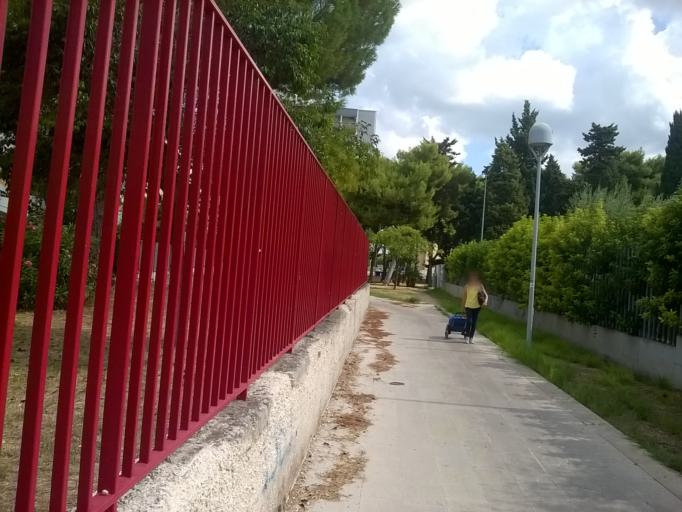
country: IT
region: Apulia
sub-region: Provincia di Taranto
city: Taranto
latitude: 40.4593
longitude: 17.2706
